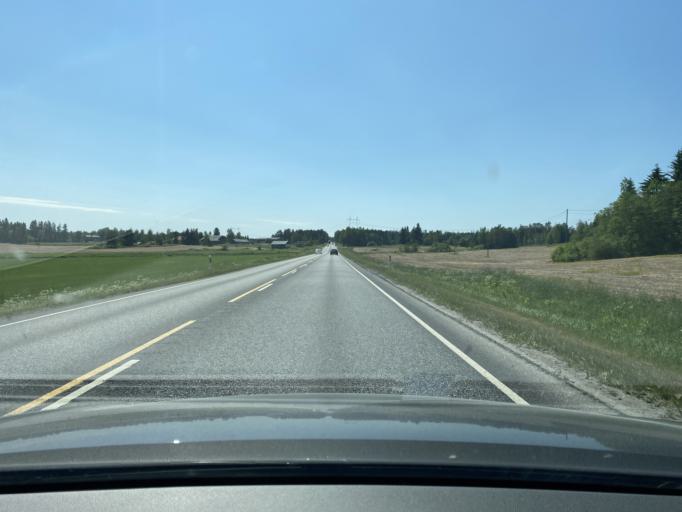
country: FI
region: Pirkanmaa
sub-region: Tampere
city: Nokia
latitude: 61.4187
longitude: 23.3255
